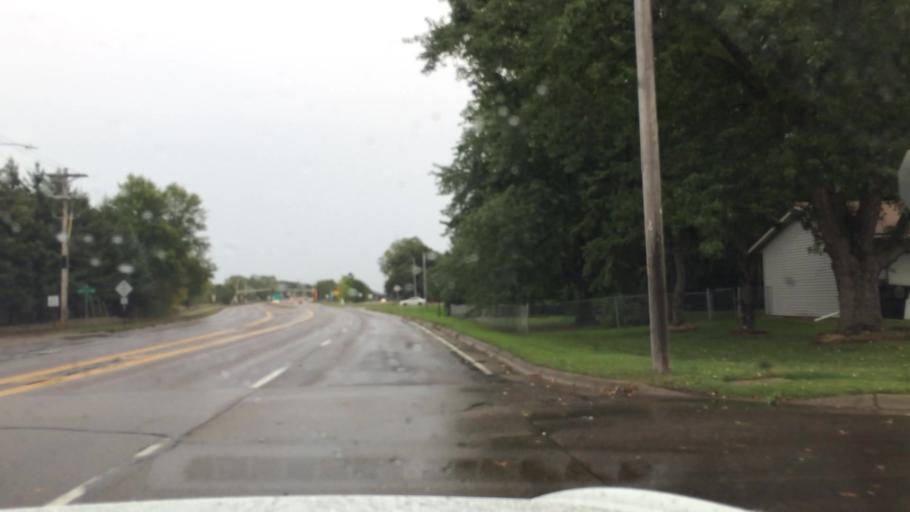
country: US
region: Minnesota
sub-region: Anoka County
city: Spring Lake Park
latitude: 45.1245
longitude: -93.2233
